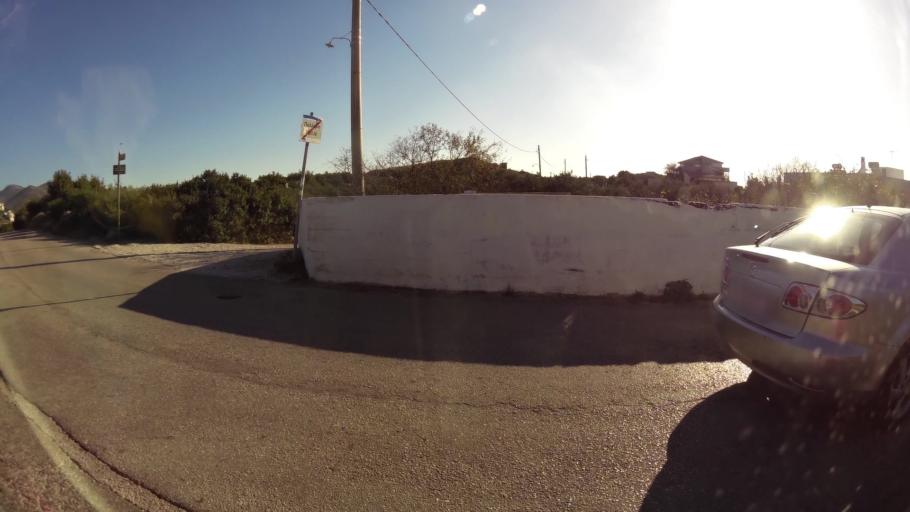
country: GR
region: Attica
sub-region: Nomarchia Anatolikis Attikis
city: Dhrafi
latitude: 38.0156
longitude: 23.9019
